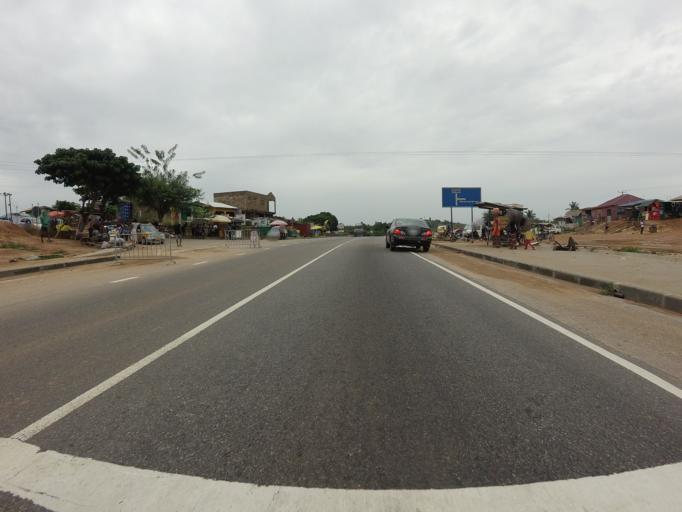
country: GH
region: Eastern
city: Nsawam
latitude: 5.9010
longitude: -0.3892
